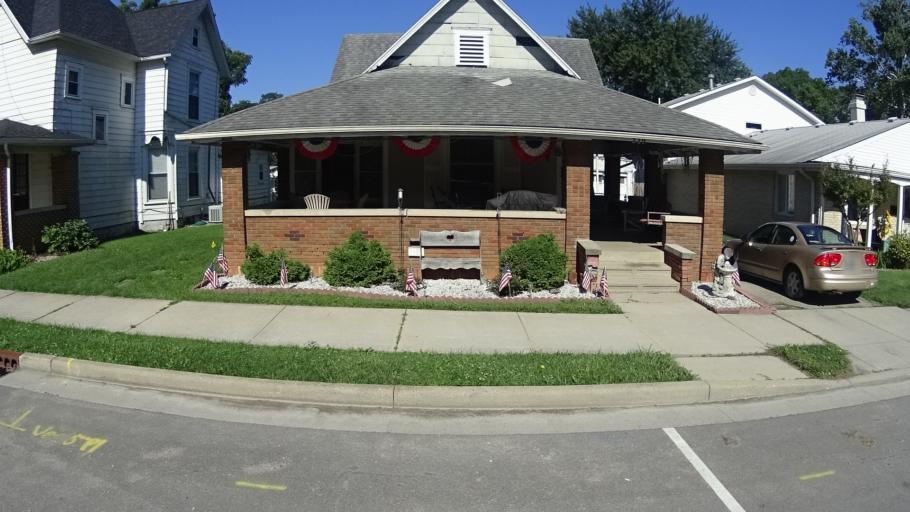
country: US
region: Indiana
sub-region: Madison County
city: Pendleton
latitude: 40.0049
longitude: -85.7457
